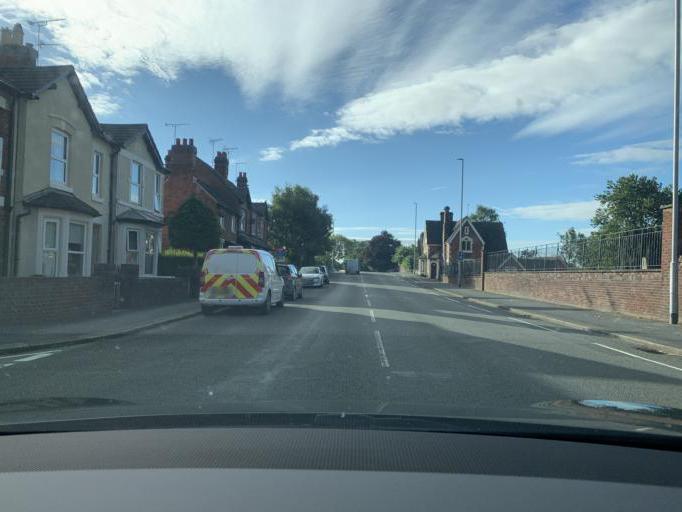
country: GB
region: England
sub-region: Staffordshire
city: Stafford
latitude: 52.8173
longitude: -2.1280
